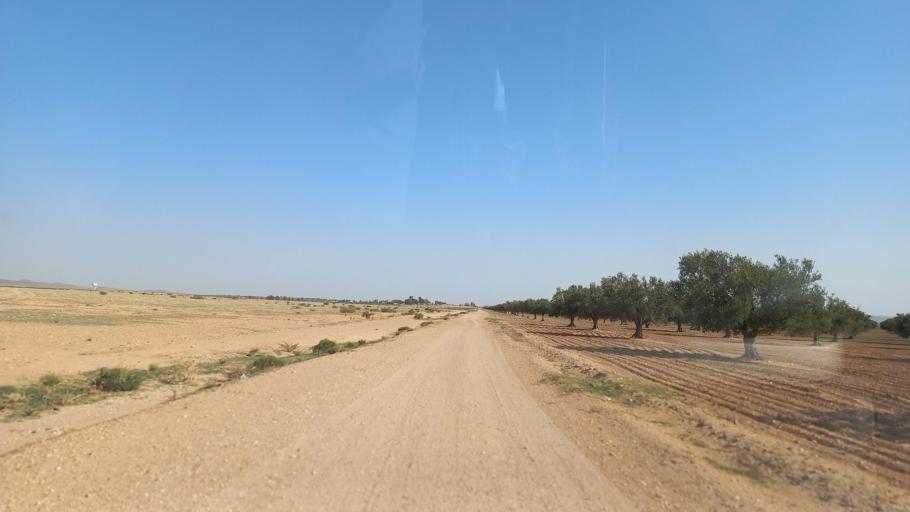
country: TN
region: Al Qasrayn
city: Kasserine
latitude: 35.3076
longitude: 9.0213
